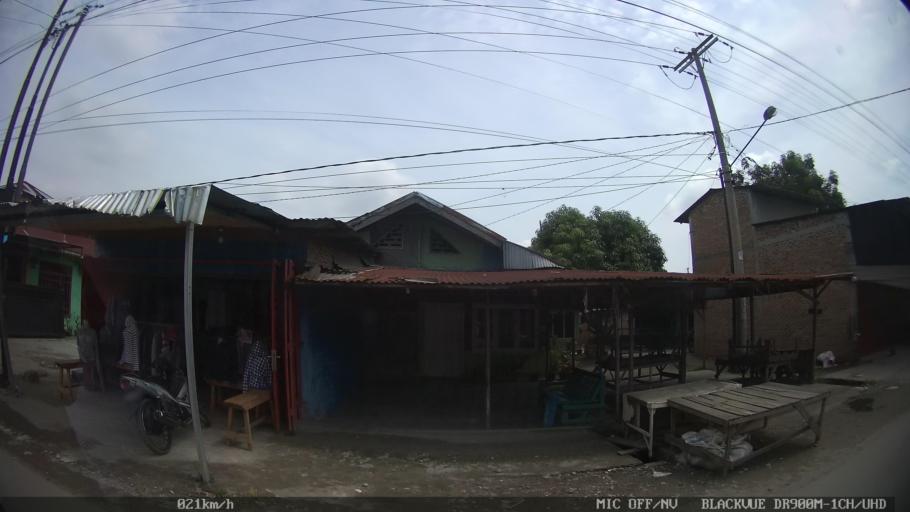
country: ID
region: North Sumatra
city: Medan
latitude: 3.6515
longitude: 98.6889
